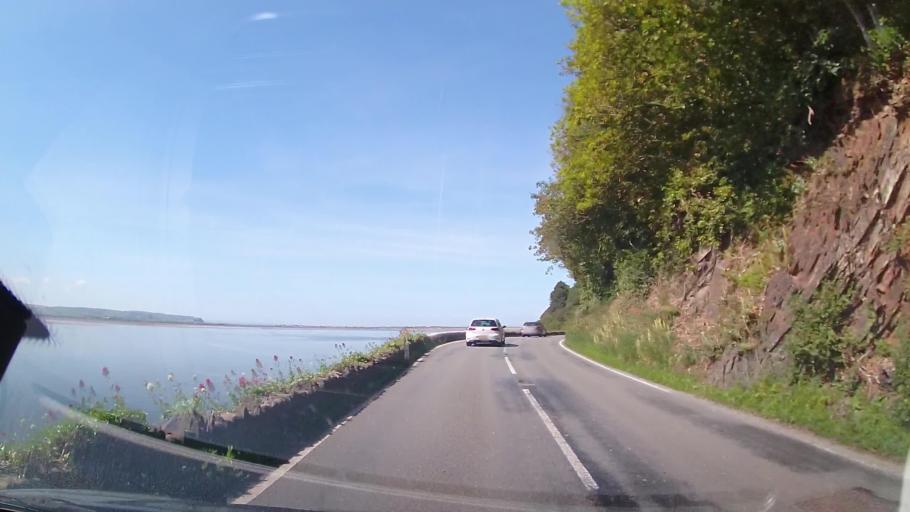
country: GB
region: Wales
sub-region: Gwynedd
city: Tywyn
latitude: 52.5506
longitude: -4.0045
